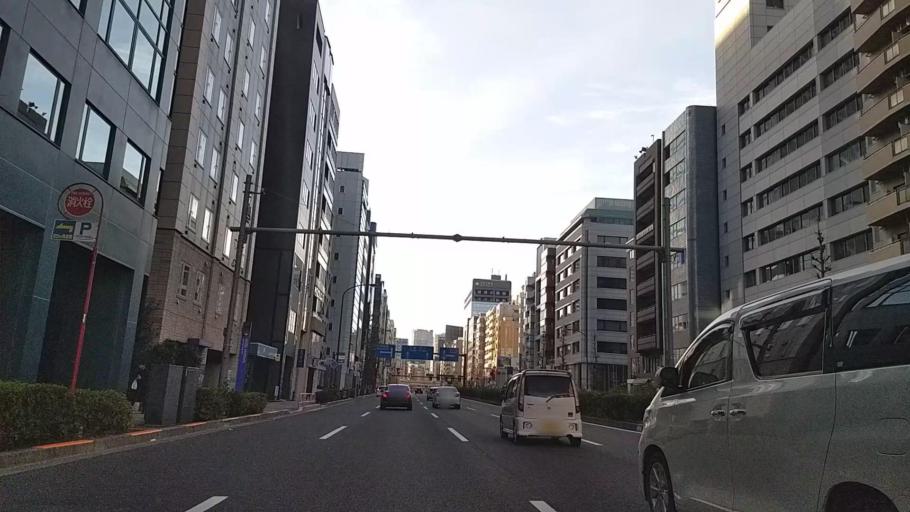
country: JP
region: Tokyo
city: Tokyo
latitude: 35.6585
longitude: 139.7550
